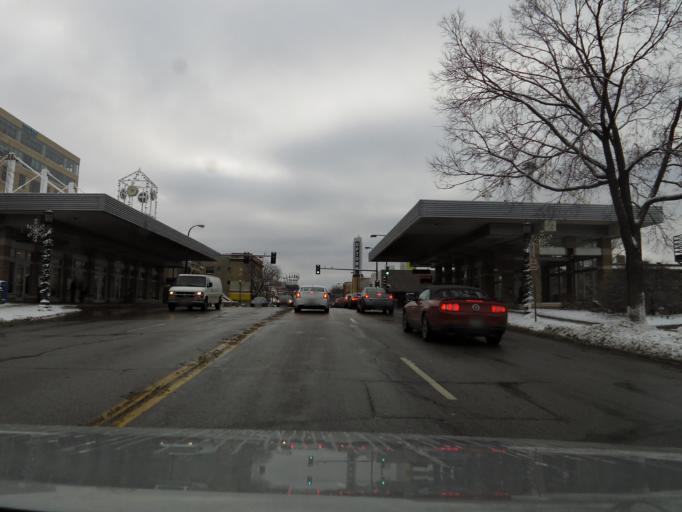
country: US
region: Minnesota
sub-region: Hennepin County
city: Minneapolis
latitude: 44.9507
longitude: -93.2983
